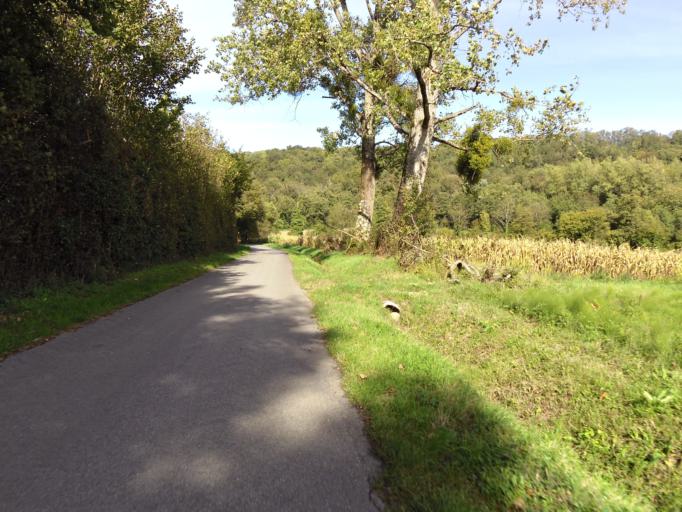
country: FR
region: Rhone-Alpes
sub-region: Departement de l'Ain
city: Perouges
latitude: 45.9242
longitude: 5.1736
